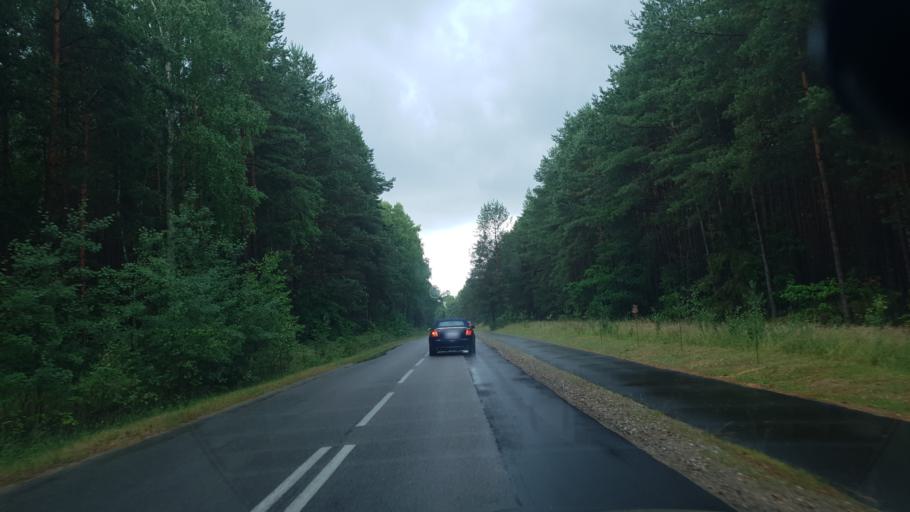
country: PL
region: Pomeranian Voivodeship
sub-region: Powiat kartuski
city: Stezyca
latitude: 54.2223
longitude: 17.9689
